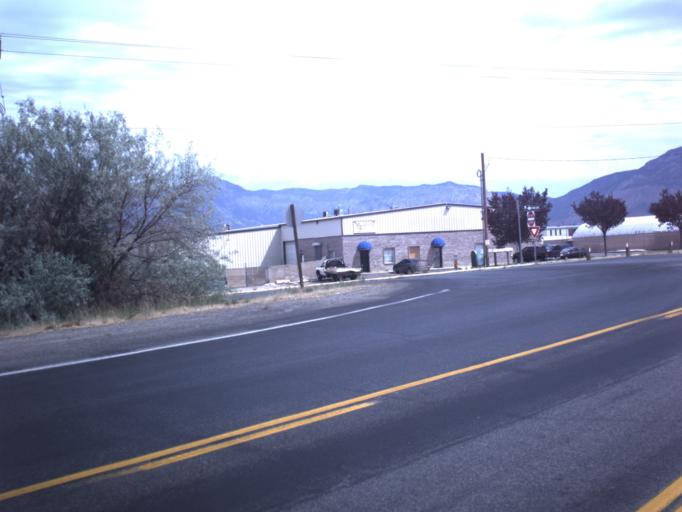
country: US
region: Utah
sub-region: Weber County
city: West Haven
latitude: 41.2046
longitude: -112.0299
